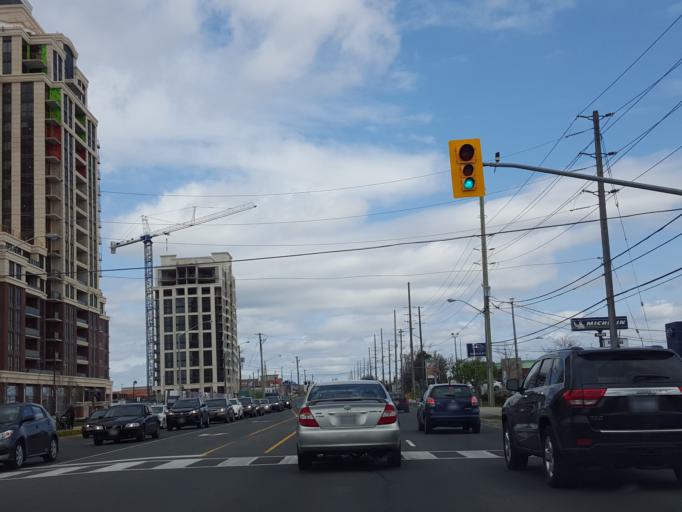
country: CA
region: Ontario
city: Markham
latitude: 43.8961
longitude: -79.2650
